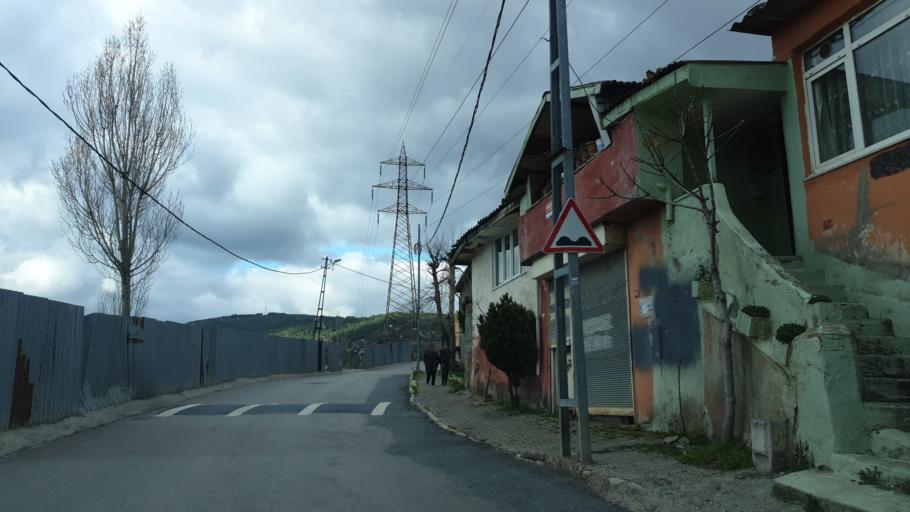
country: TR
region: Istanbul
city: Pendik
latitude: 40.8976
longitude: 29.2369
